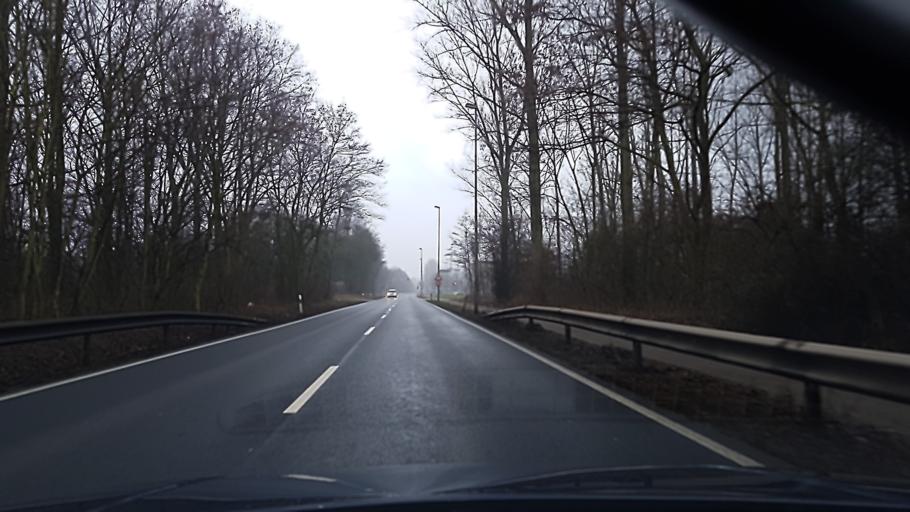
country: DE
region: Lower Saxony
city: Cramme
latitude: 52.1581
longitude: 10.4261
